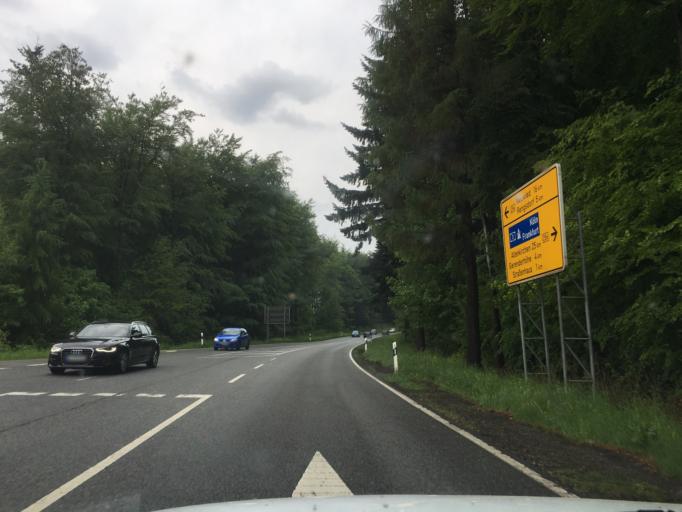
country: DE
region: Rheinland-Pfalz
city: Bonefeld
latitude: 50.5377
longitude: 7.5121
